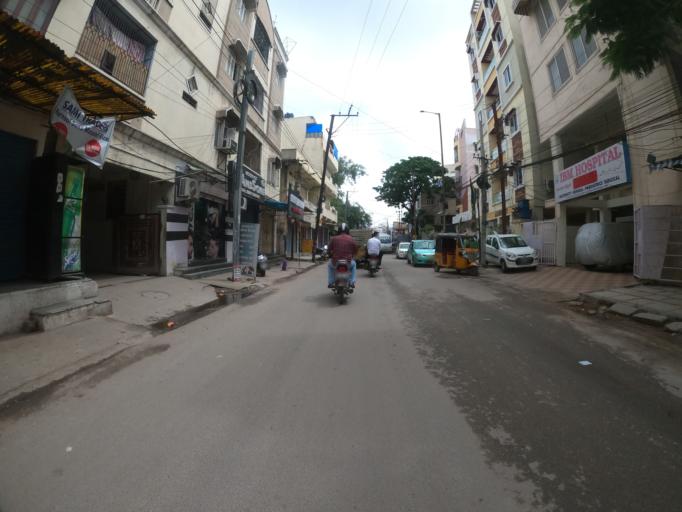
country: IN
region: Telangana
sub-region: Hyderabad
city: Hyderabad
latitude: 17.3957
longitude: 78.4174
